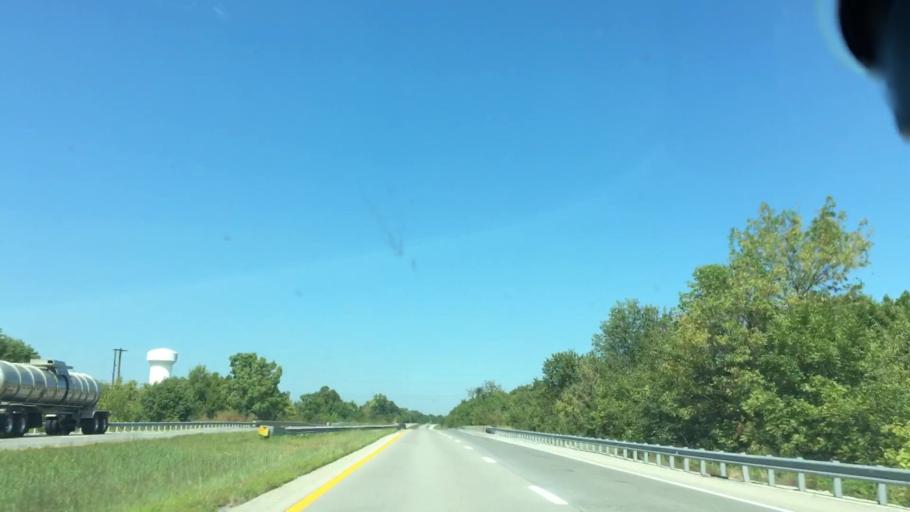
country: US
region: Kentucky
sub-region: Webster County
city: Sebree
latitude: 37.6470
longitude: -87.5115
